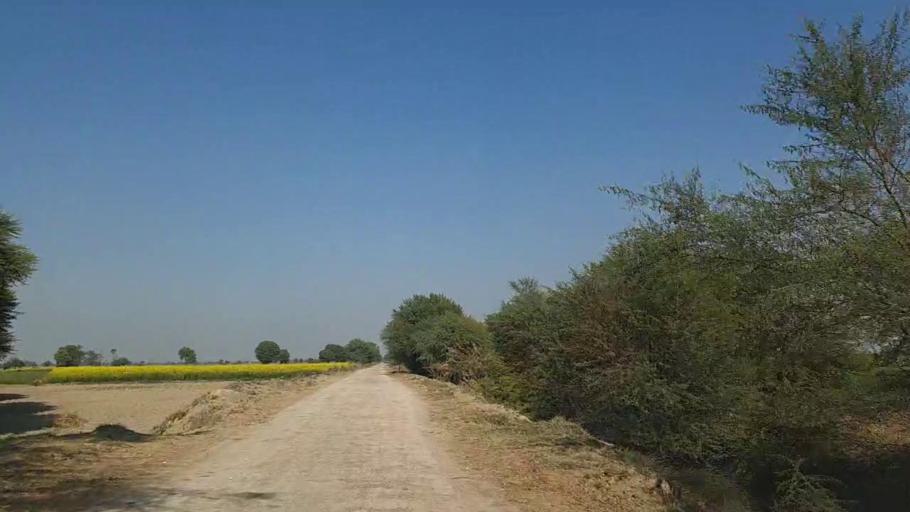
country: PK
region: Sindh
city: Shahpur Chakar
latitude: 26.1820
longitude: 68.6001
